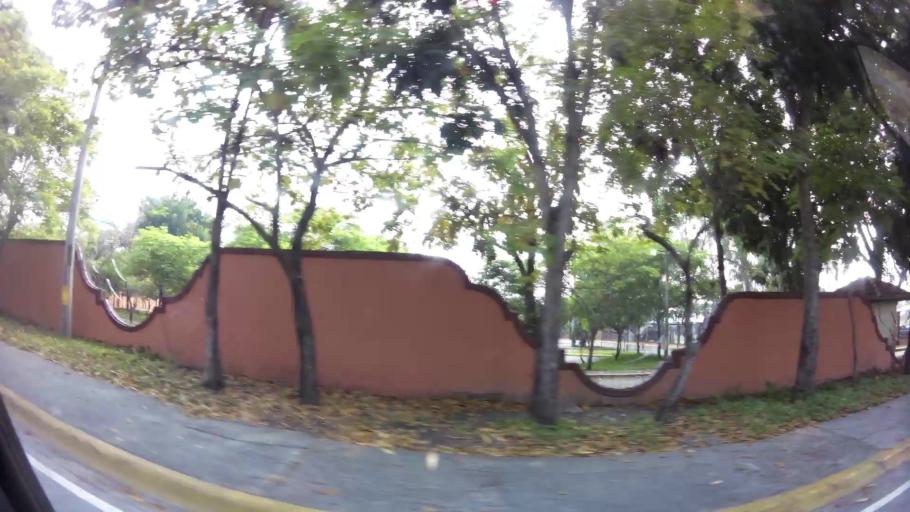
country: HN
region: Cortes
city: El Zapotal del Norte
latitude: 15.5234
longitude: -88.0365
